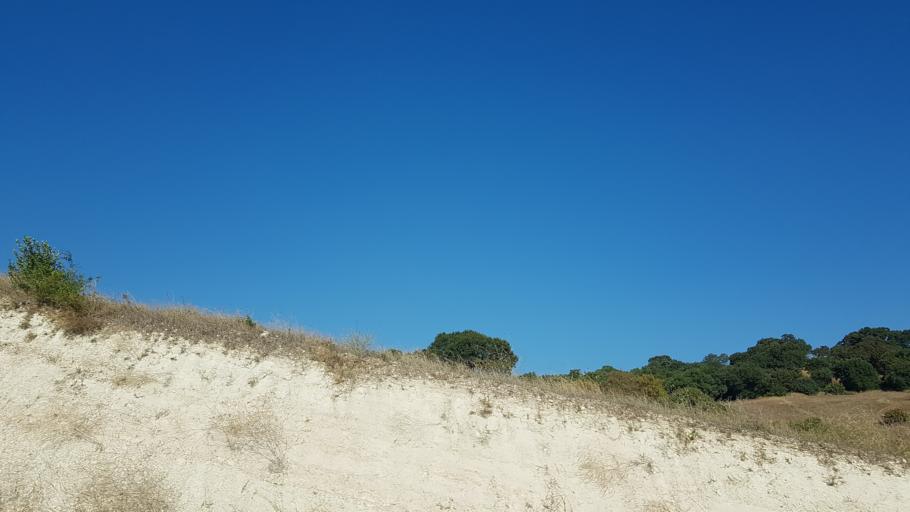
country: TR
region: Balikesir
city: Ertugrul
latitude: 39.5838
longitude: 27.6972
